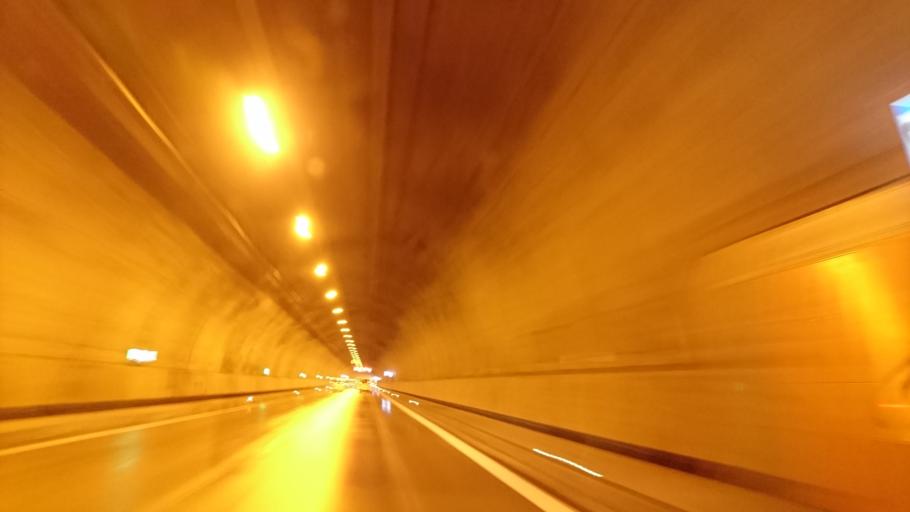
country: DE
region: Bavaria
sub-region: Upper Palatinate
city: Lappersdorf
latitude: 49.0352
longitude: 12.0859
